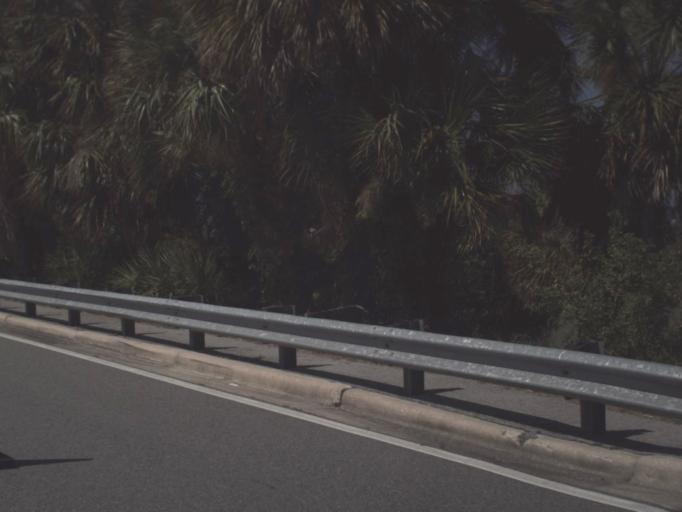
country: US
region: Florida
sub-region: Brevard County
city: Melbourne
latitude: 28.1133
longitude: -80.6196
